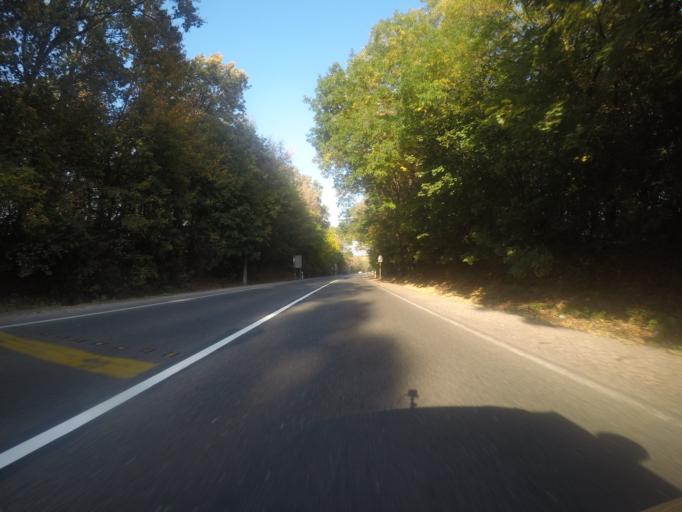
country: HU
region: Fejer
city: dunaujvaros
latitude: 46.9818
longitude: 18.9129
